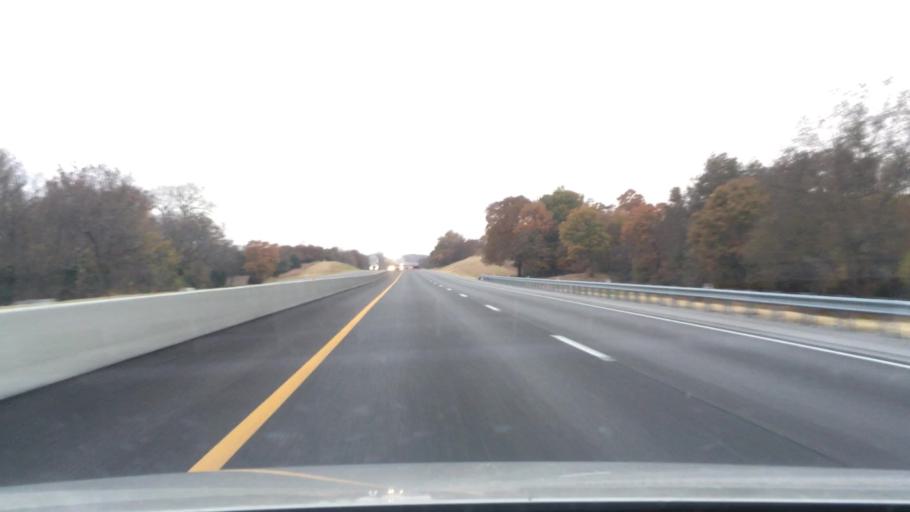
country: US
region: Oklahoma
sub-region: Lincoln County
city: Stroud
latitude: 35.7425
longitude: -96.7494
